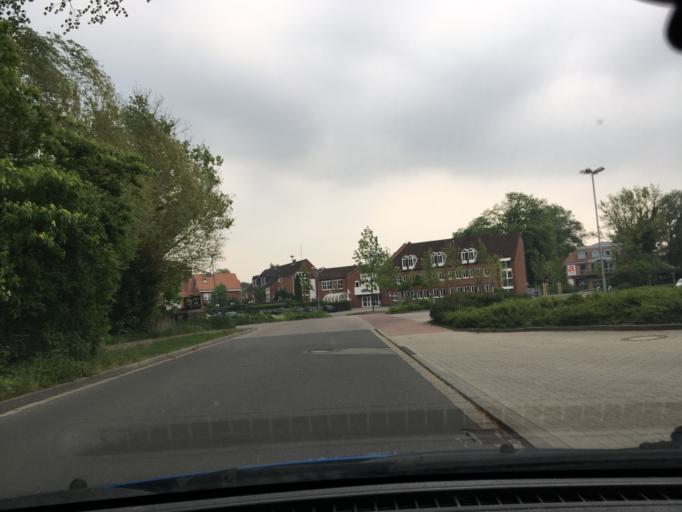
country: DE
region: Lower Saxony
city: Seevetal
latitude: 53.3862
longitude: 9.9793
